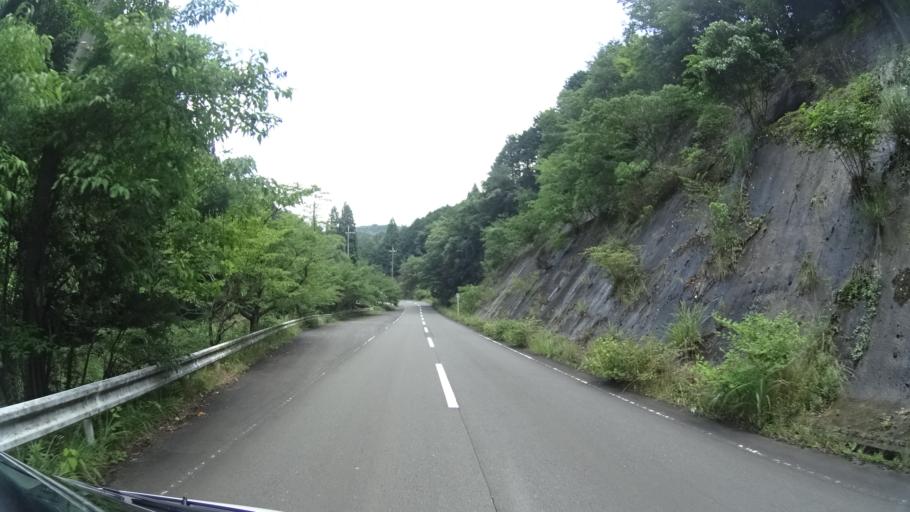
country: JP
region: Kyoto
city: Ayabe
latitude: 35.1887
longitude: 135.2433
